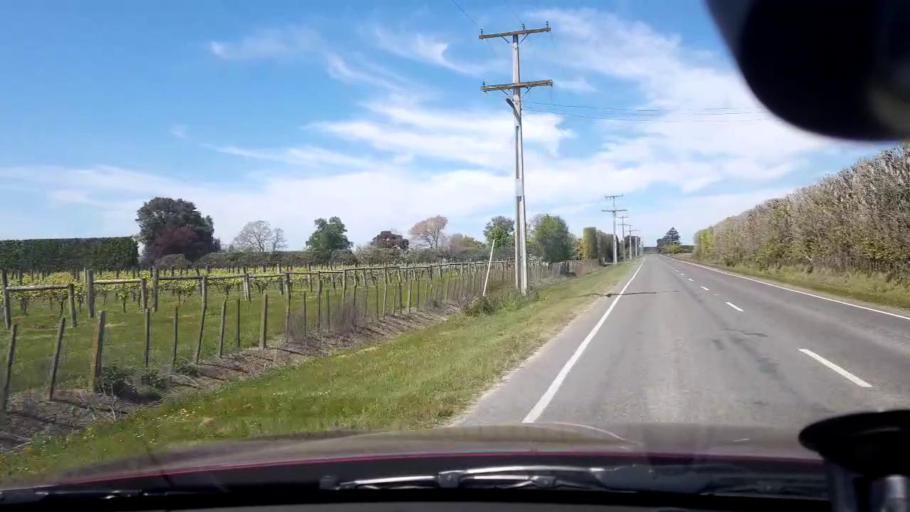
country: NZ
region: Gisborne
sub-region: Gisborne District
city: Gisborne
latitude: -38.6329
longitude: 177.9285
